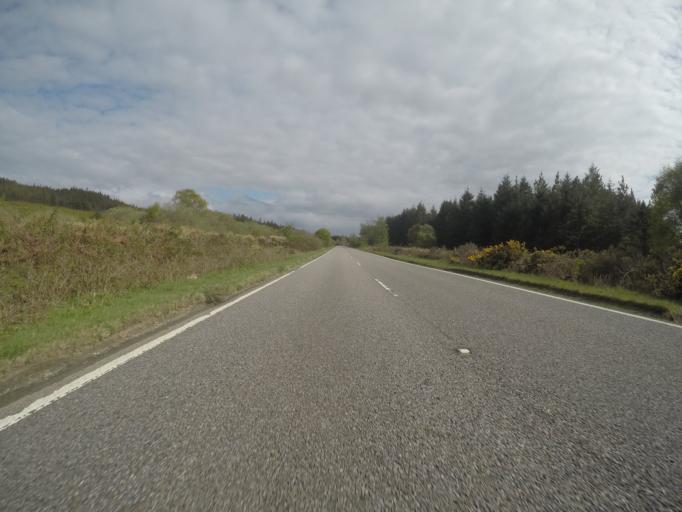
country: GB
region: Scotland
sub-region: Highland
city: Portree
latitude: 57.2483
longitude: -5.9310
